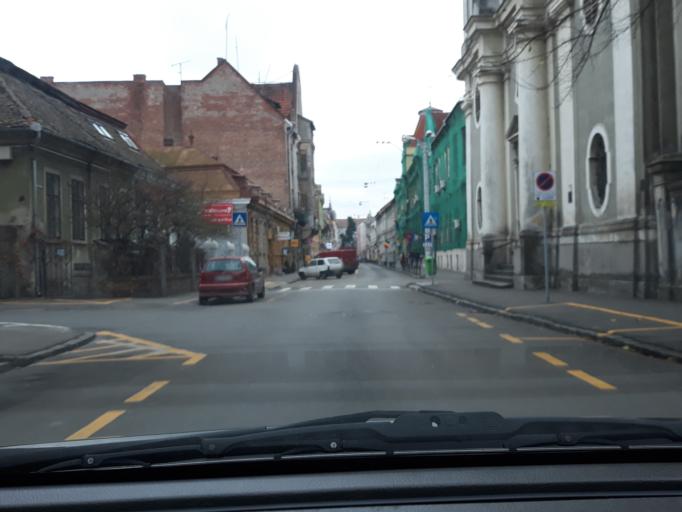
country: RO
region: Bihor
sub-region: Comuna Biharea
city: Oradea
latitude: 47.0603
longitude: 21.9315
